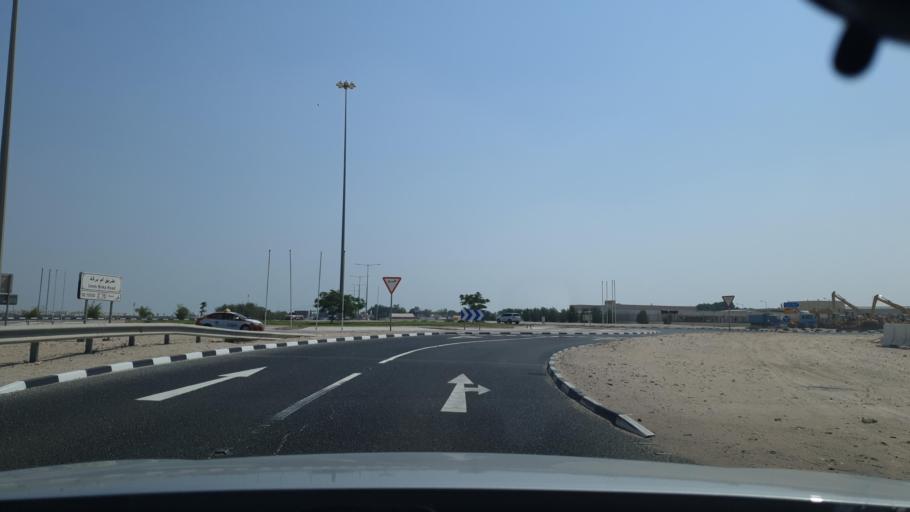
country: QA
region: Al Khawr
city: Al Khawr
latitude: 25.7219
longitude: 51.4990
